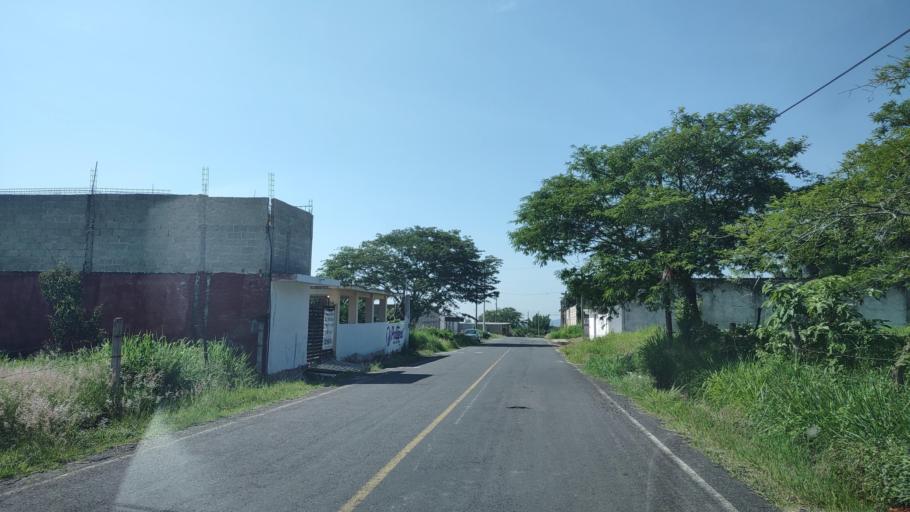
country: MX
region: Veracruz
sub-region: Emiliano Zapata
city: Dos Rios
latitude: 19.4919
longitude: -96.8222
